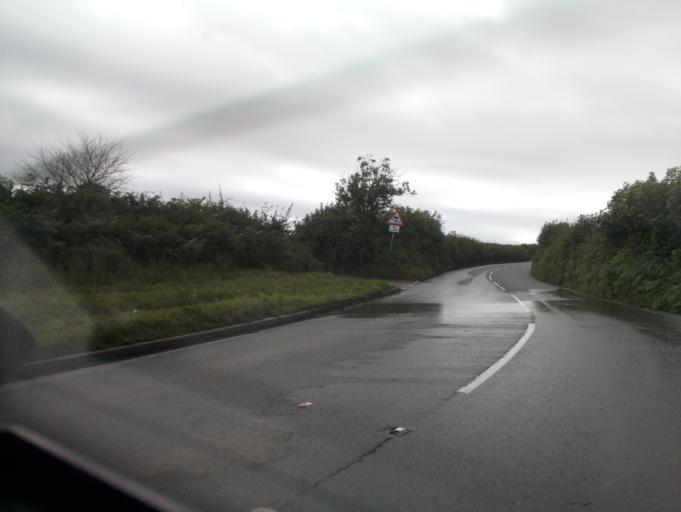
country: GB
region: England
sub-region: Devon
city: Kingsbridge
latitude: 50.2952
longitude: -3.7888
